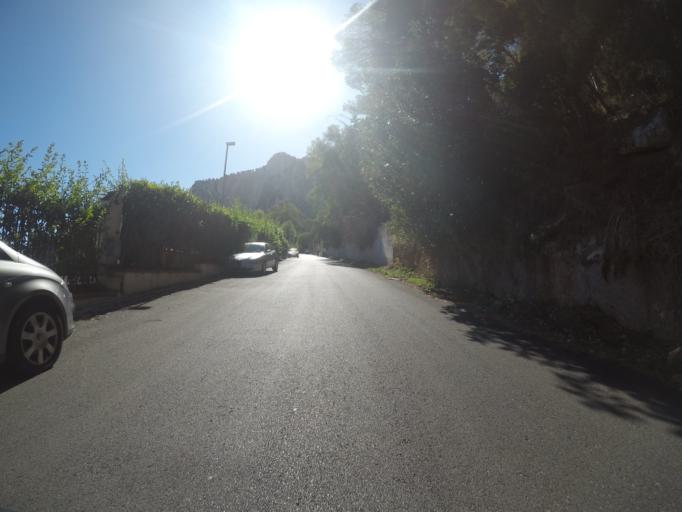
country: IT
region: Sicily
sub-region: Palermo
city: Palermo
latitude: 38.1897
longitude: 13.3400
